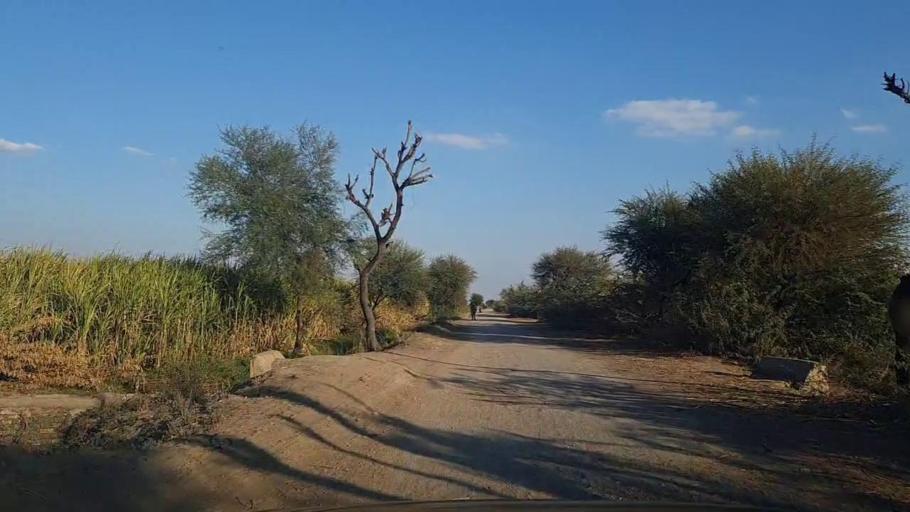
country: PK
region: Sindh
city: Jhol
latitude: 25.9269
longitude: 69.0118
